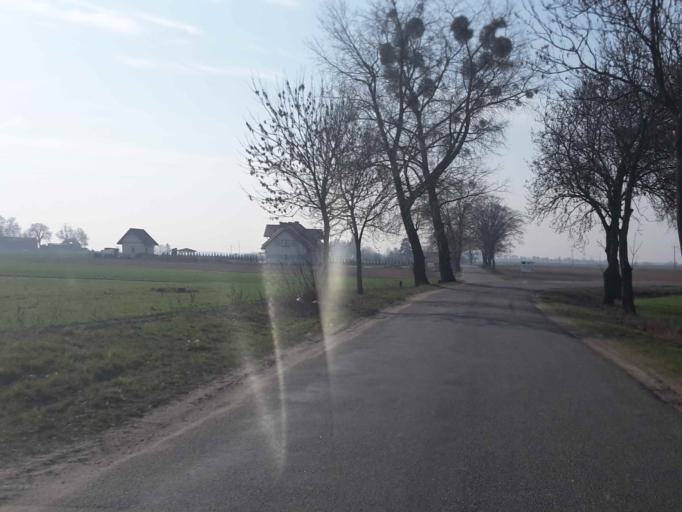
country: PL
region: Kujawsko-Pomorskie
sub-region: Powiat brodnicki
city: Bobrowo
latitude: 53.2267
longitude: 19.2546
